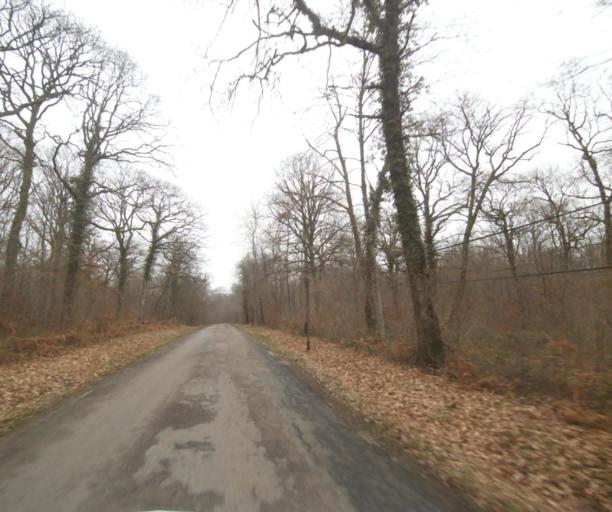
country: FR
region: Champagne-Ardenne
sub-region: Departement de la Haute-Marne
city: Wassy
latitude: 48.5219
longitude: 4.9747
